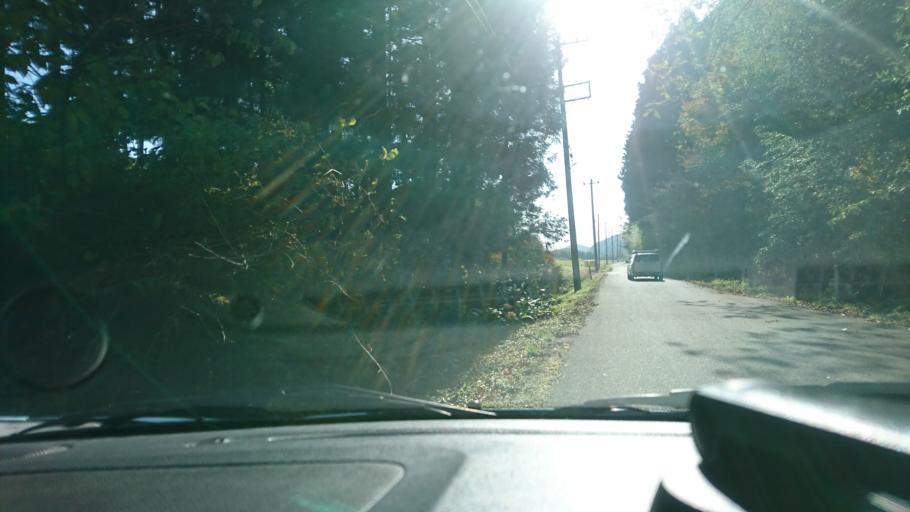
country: JP
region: Iwate
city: Ichinoseki
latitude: 38.8172
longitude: 141.2504
